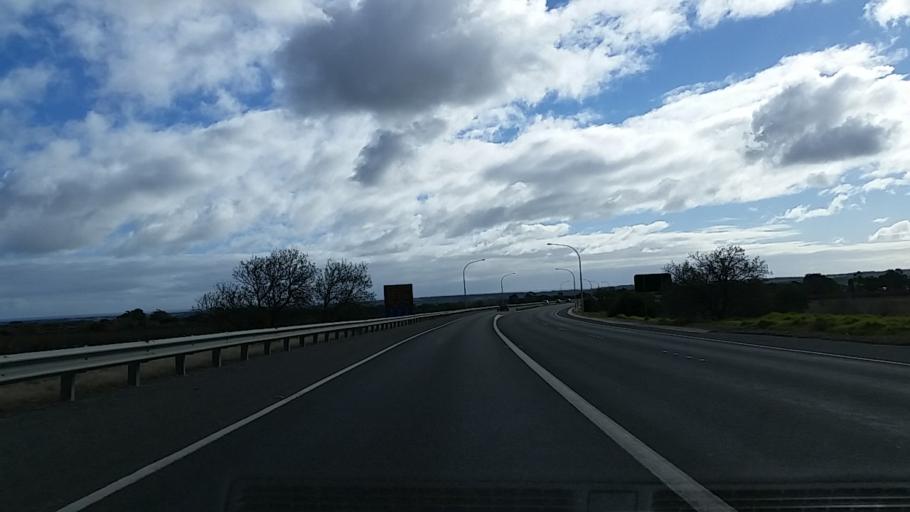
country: AU
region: South Australia
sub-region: Onkaparinga
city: McLaren Vale
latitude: -35.2771
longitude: 138.5450
